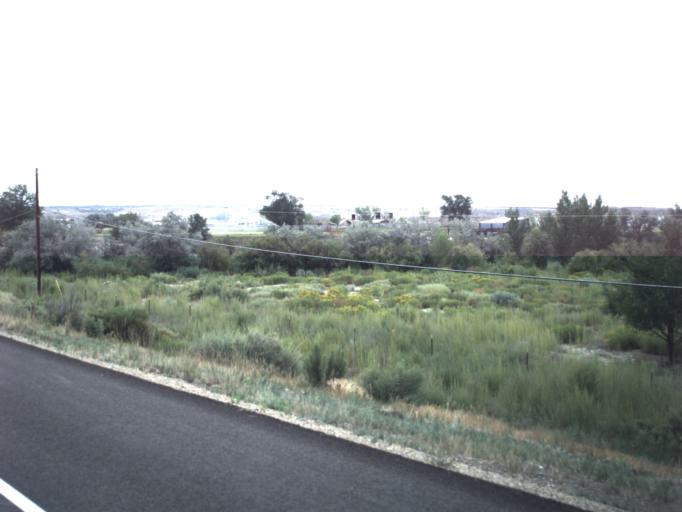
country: US
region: Utah
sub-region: Carbon County
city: Wellington
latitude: 39.5425
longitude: -110.7014
